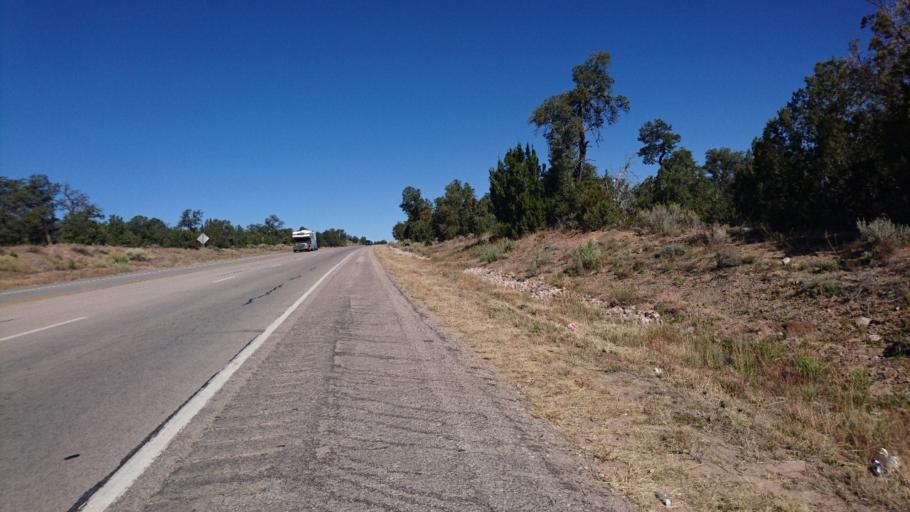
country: US
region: New Mexico
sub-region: McKinley County
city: Black Rock
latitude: 35.2236
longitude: -108.7660
